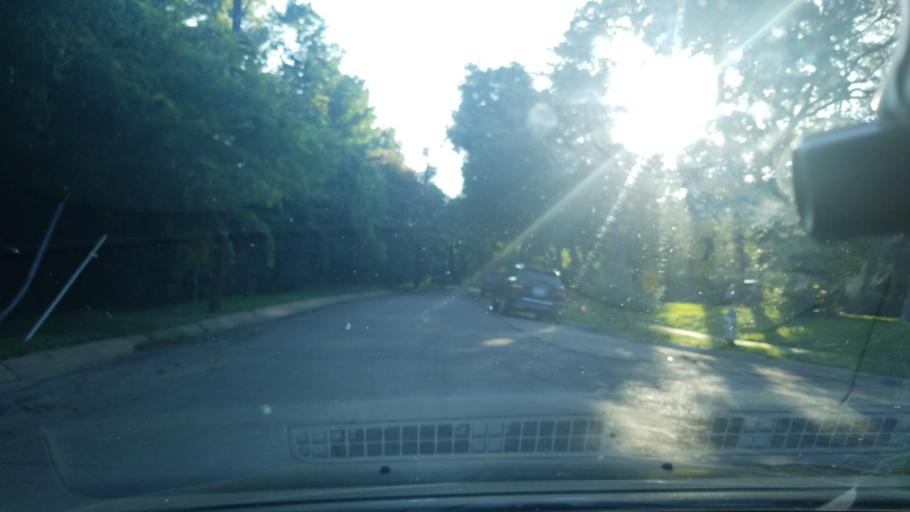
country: US
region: Texas
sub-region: Dallas County
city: Dallas
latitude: 32.7320
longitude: -96.8214
